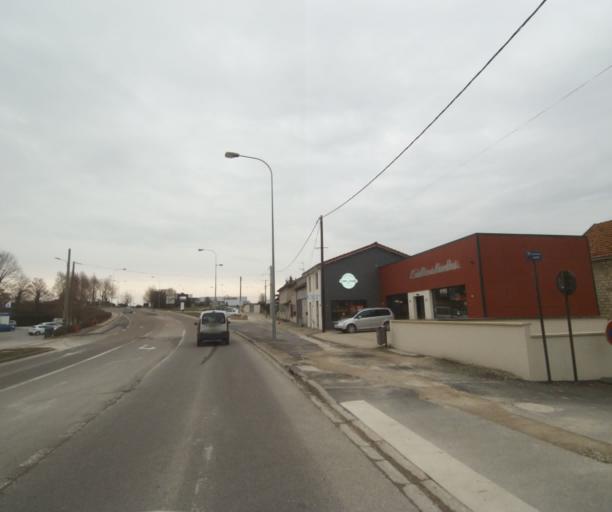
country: FR
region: Champagne-Ardenne
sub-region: Departement de la Haute-Marne
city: Saint-Dizier
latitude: 48.6270
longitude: 4.9607
